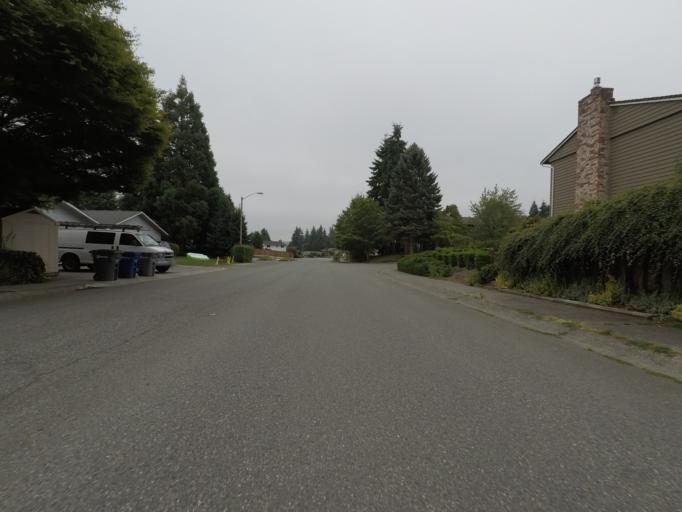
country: US
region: Washington
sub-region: King County
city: Bothell
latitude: 47.7693
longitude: -122.2208
